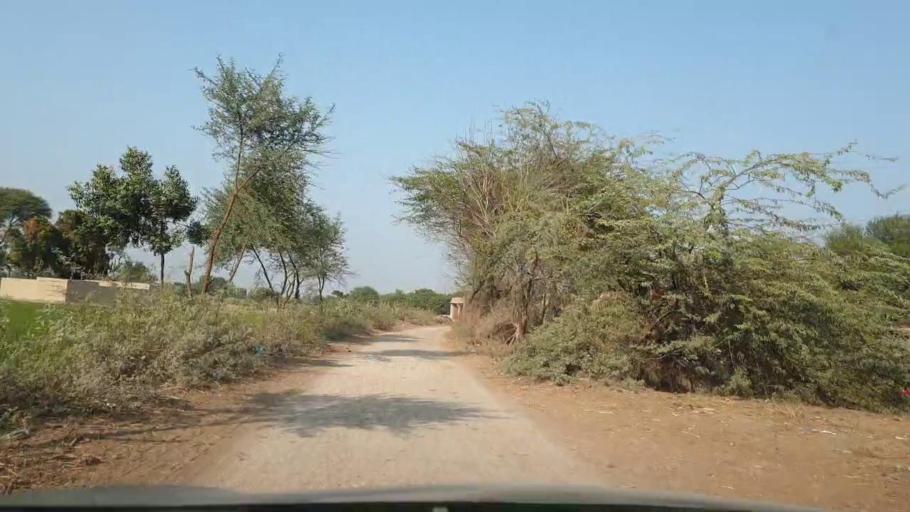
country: PK
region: Sindh
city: Tando Allahyar
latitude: 25.5540
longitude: 68.7936
